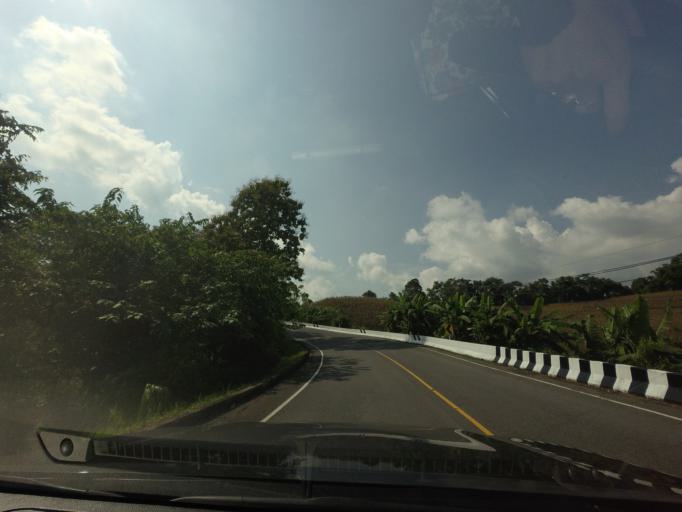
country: TH
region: Nan
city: Santi Suk
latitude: 18.9824
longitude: 100.9986
